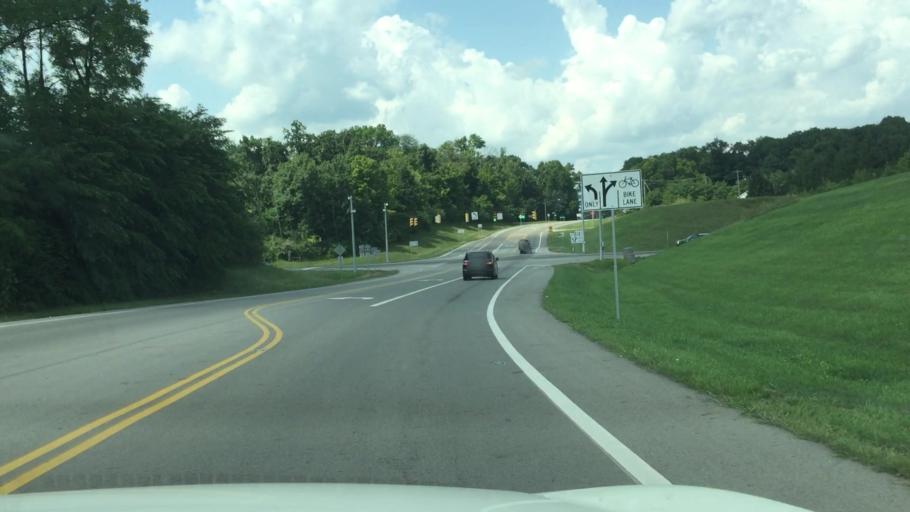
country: US
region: Ohio
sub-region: Clark County
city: Northridge
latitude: 39.9783
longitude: -83.7842
